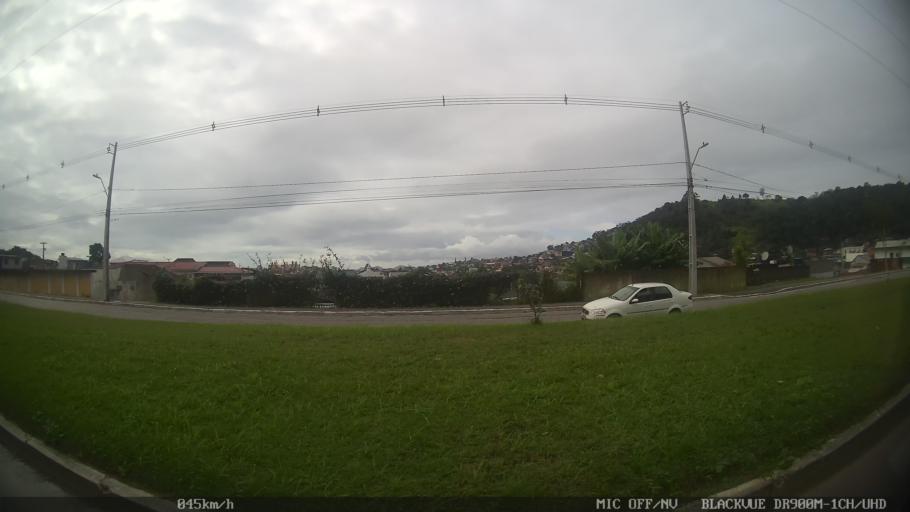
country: BR
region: Santa Catarina
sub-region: Biguacu
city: Biguacu
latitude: -27.5484
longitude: -48.6465
